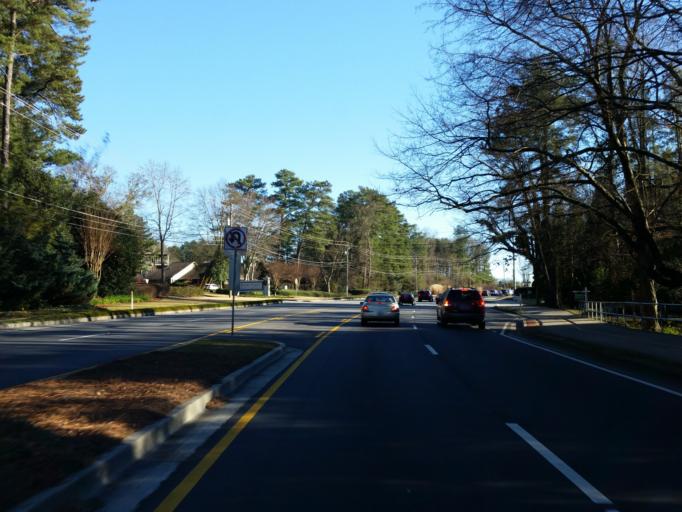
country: US
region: Georgia
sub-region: Cobb County
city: Smyrna
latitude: 33.8707
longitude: -84.4958
